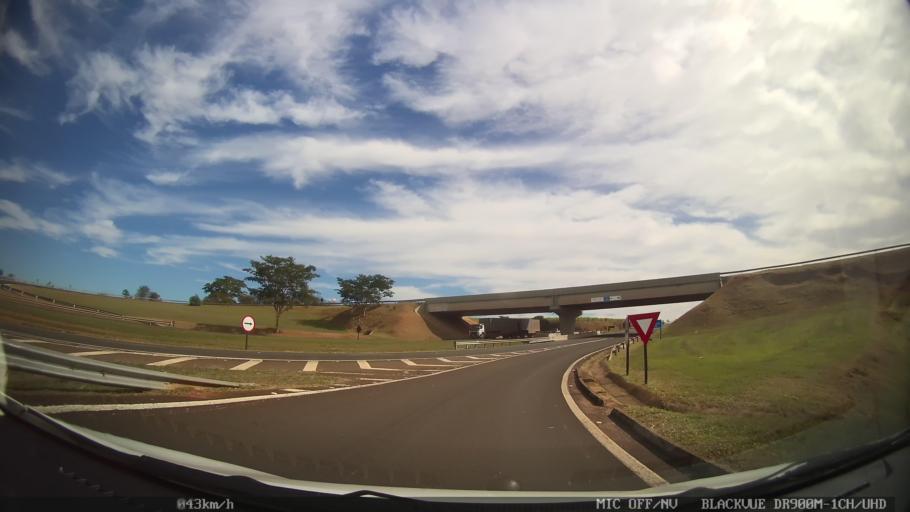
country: BR
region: Sao Paulo
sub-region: Taquaritinga
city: Taquaritinga
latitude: -21.5156
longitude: -48.5405
